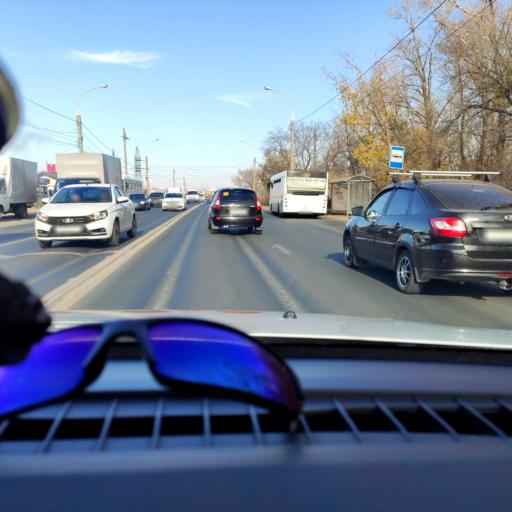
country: RU
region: Samara
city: Samara
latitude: 53.1312
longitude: 50.1725
